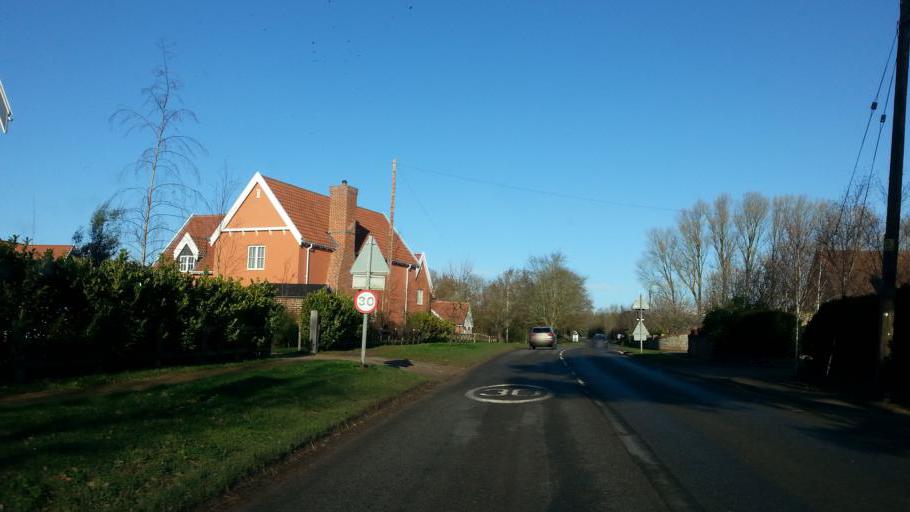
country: GB
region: England
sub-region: Suffolk
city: Saxmundham
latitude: 52.1733
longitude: 1.5011
